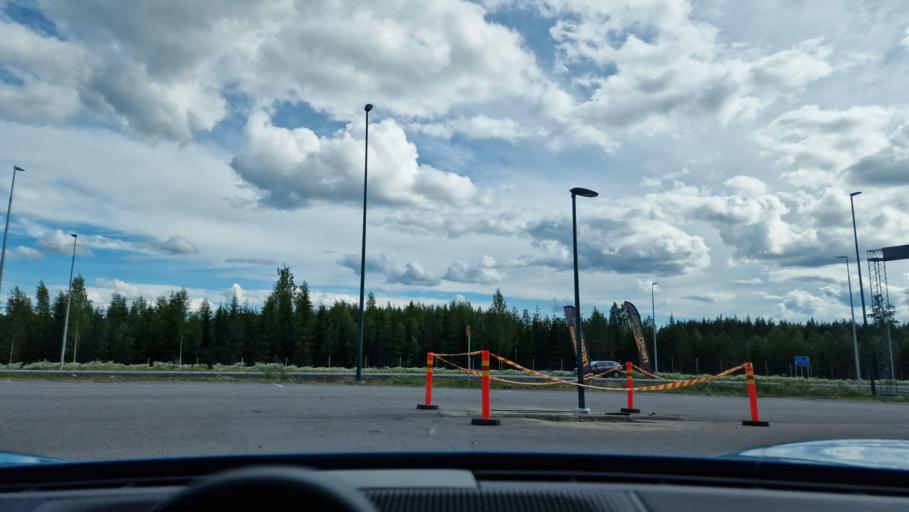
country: FI
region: Pirkanmaa
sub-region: Tampere
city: Orivesi
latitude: 61.6707
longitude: 24.2851
